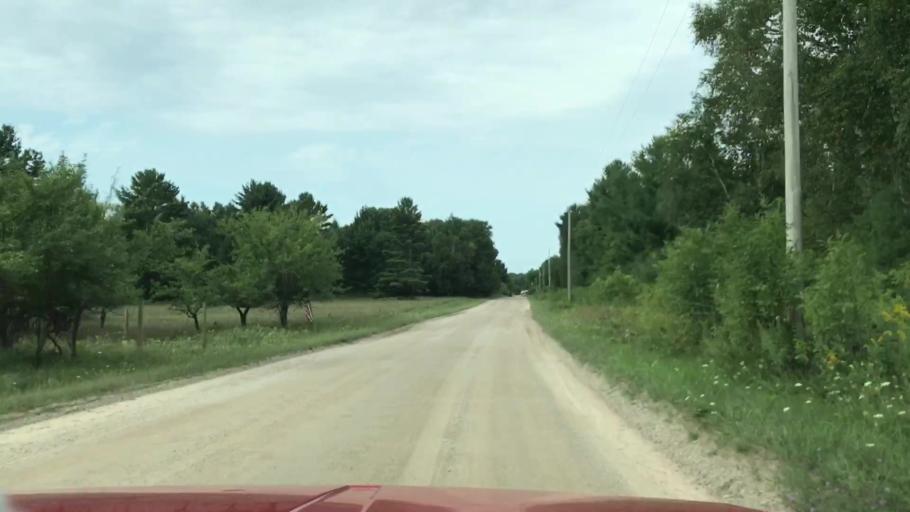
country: US
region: Michigan
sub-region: Charlevoix County
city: Charlevoix
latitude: 45.7248
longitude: -85.5517
